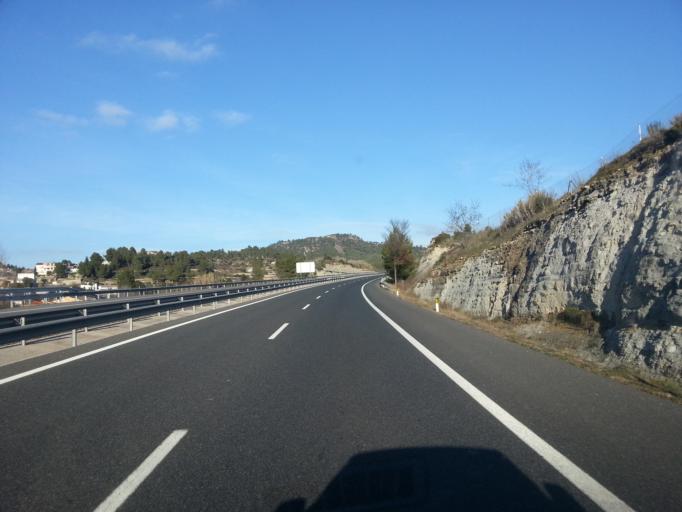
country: ES
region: Catalonia
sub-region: Provincia de Barcelona
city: Monistrol de Montserrat
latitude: 41.6581
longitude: 1.8689
